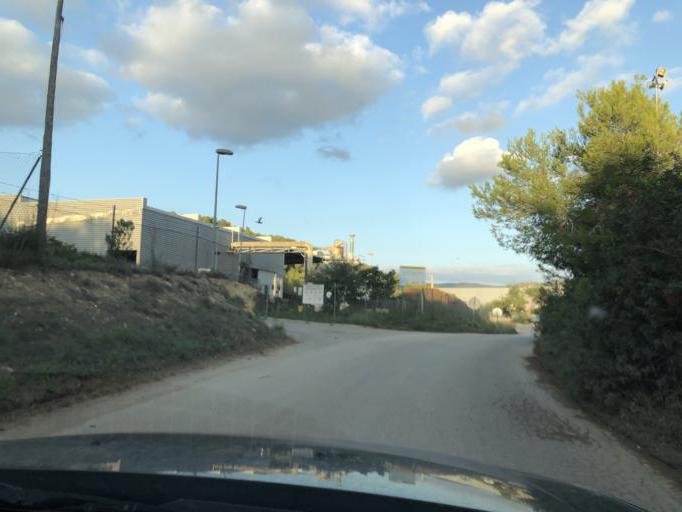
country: ES
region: Balearic Islands
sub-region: Illes Balears
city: Santa Ponsa
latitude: 39.5383
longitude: 2.4830
